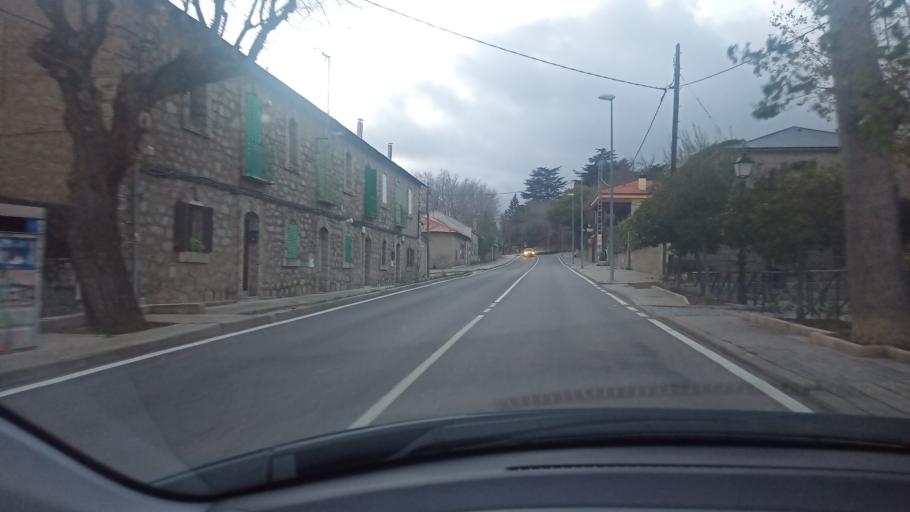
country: ES
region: Madrid
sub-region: Provincia de Madrid
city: Zarzalejo
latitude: 40.5398
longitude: -4.1568
